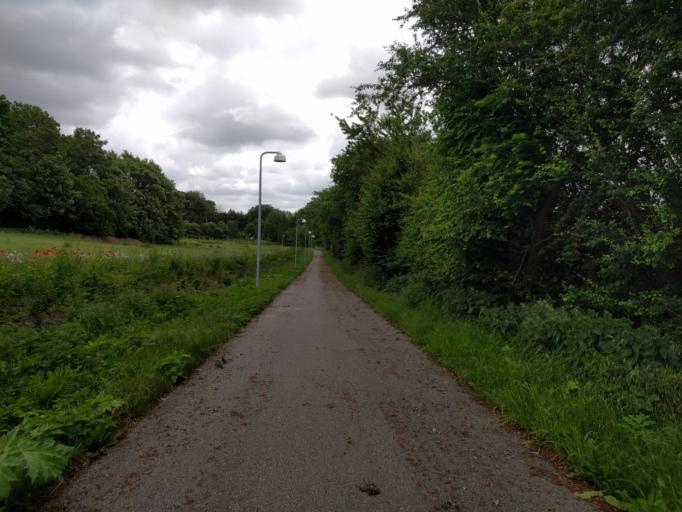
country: DK
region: South Denmark
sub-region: Odense Kommune
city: Bullerup
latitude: 55.4036
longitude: 10.4624
